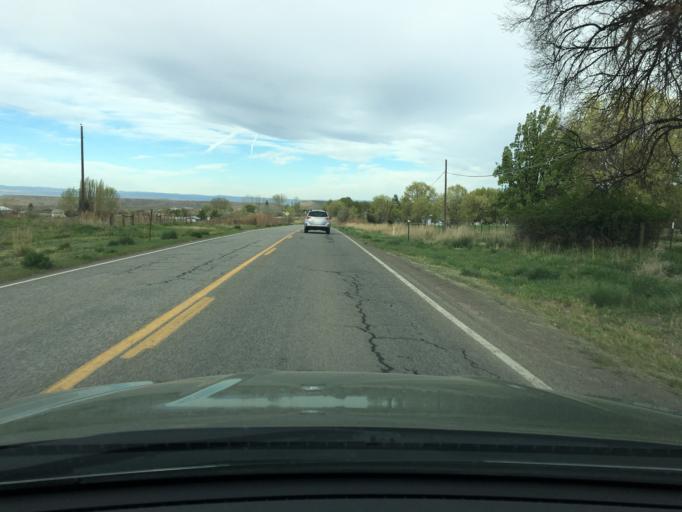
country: US
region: Colorado
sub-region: Delta County
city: Cedaredge
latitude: 38.8004
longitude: -107.8012
